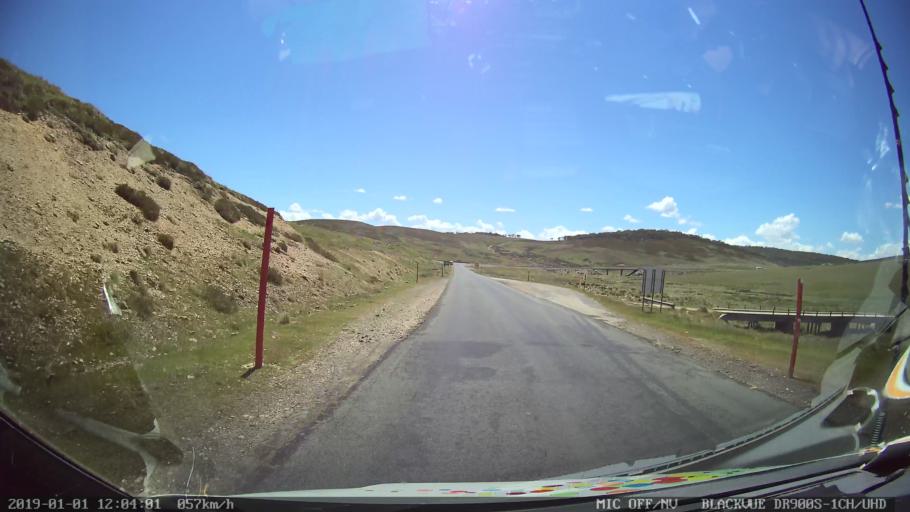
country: AU
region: New South Wales
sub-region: Snowy River
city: Jindabyne
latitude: -35.8686
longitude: 148.4931
